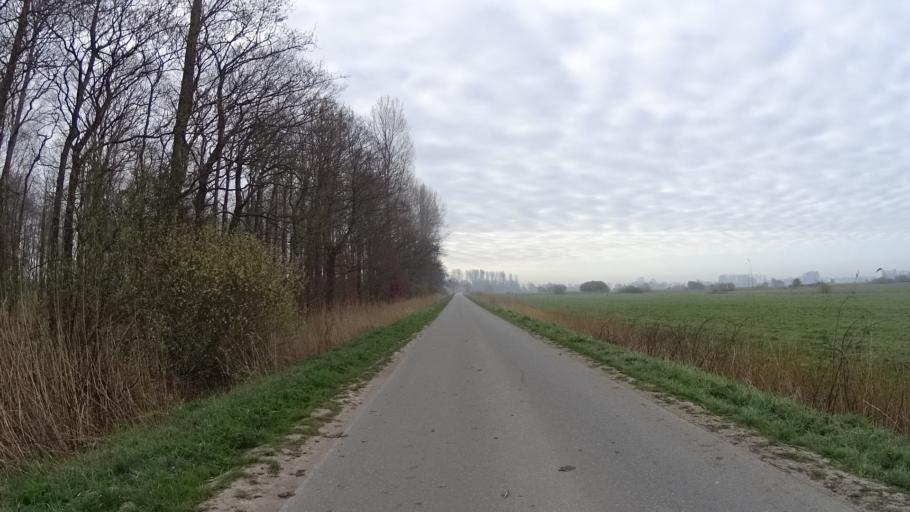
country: DE
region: Lower Saxony
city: Upgant-Schott
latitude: 53.4556
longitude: 7.3277
